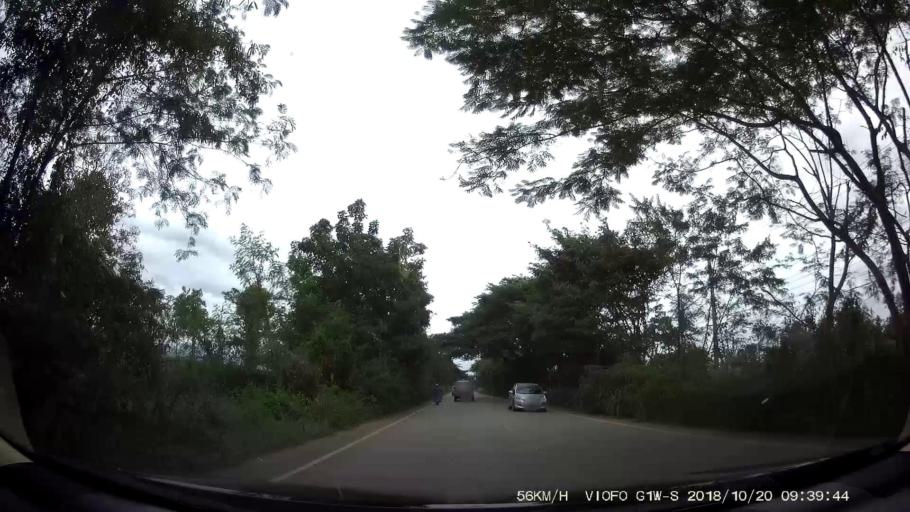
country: TH
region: Chaiyaphum
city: Kaset Sombun
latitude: 16.4371
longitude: 101.9641
